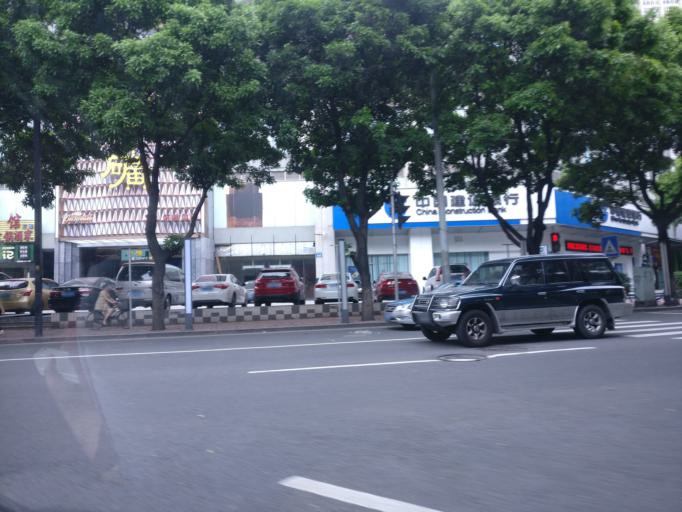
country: CN
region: Guangdong
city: Guangzhou
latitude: 23.1016
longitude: 113.2781
